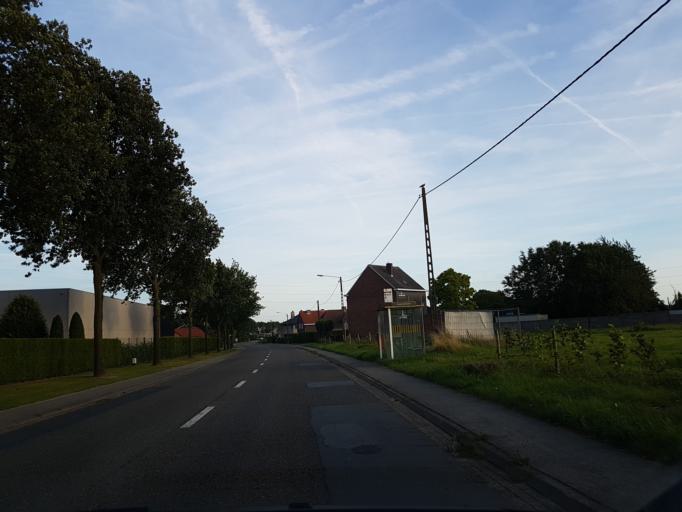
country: BE
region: Flanders
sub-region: Provincie Vlaams-Brabant
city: Merchtem
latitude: 50.9751
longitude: 4.2311
